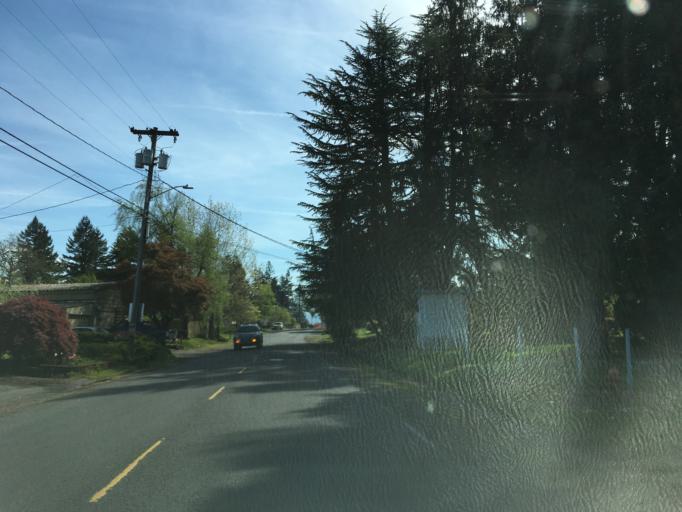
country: US
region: Oregon
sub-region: Multnomah County
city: Lents
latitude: 45.5372
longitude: -122.5222
